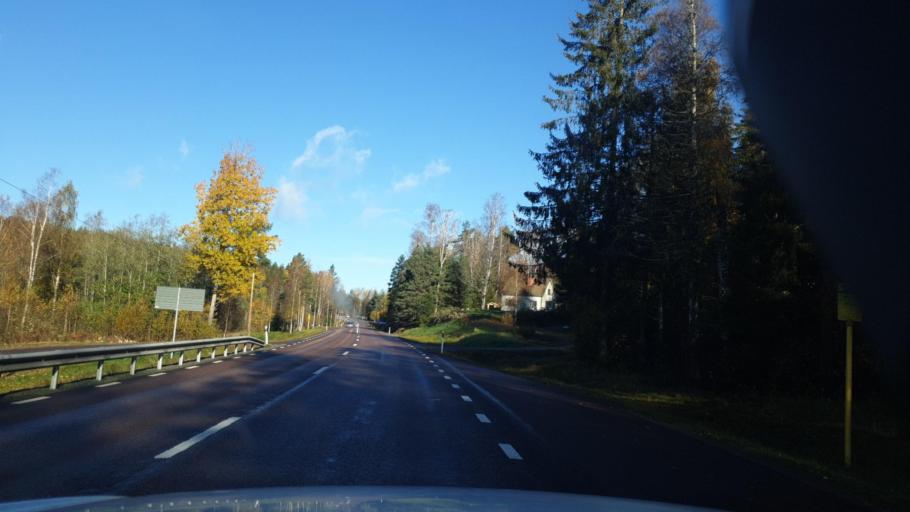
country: SE
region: Vaermland
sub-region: Sunne Kommun
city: Sunne
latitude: 59.6510
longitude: 12.9453
